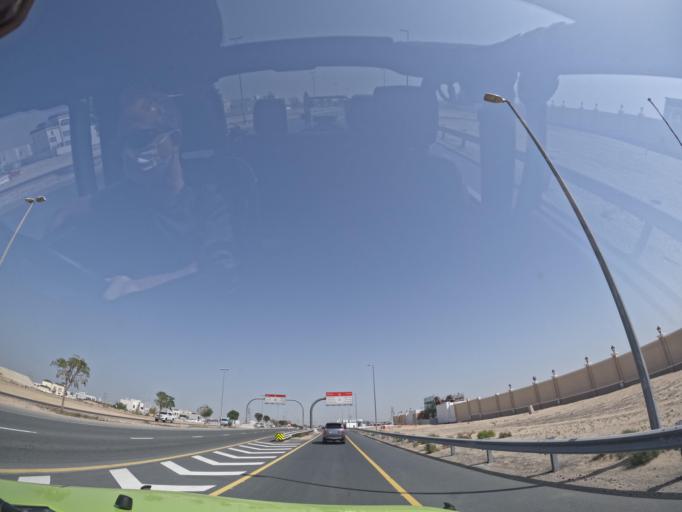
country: AE
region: Ash Shariqah
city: Sharjah
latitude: 25.1559
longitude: 55.3629
